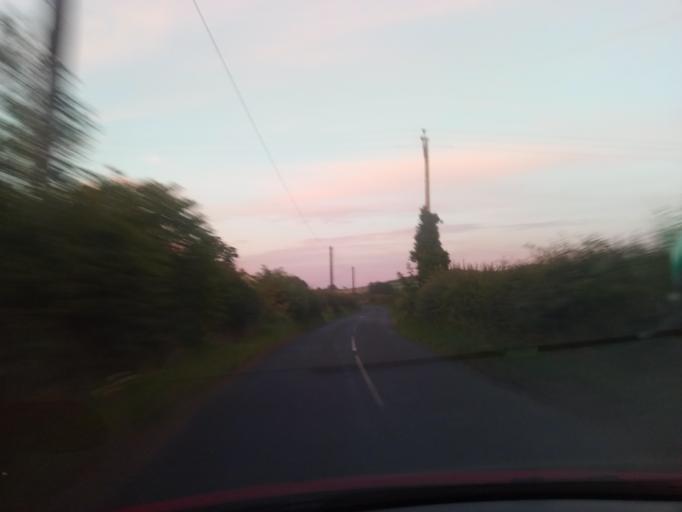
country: GB
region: England
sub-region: Northumberland
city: Warden
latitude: 54.9793
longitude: -2.2345
